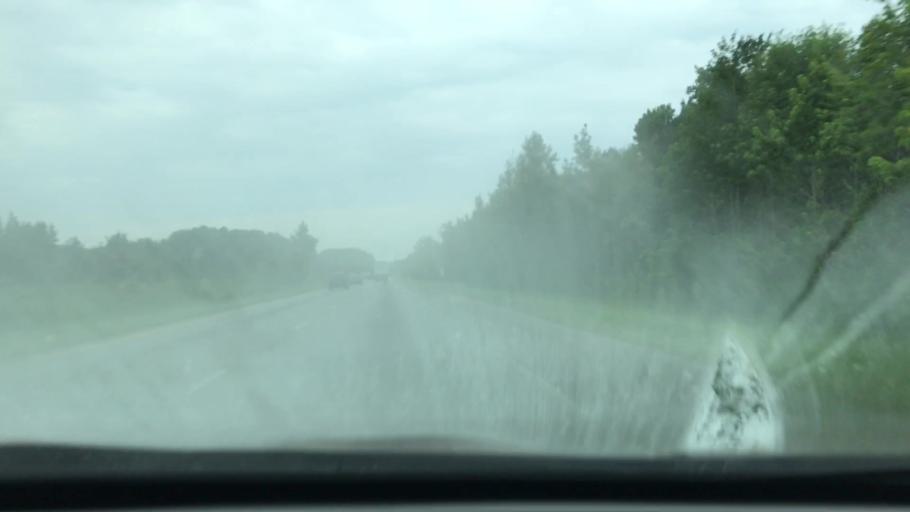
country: US
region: South Carolina
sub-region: Jasper County
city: Ridgeland
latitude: 32.5095
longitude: -80.9686
